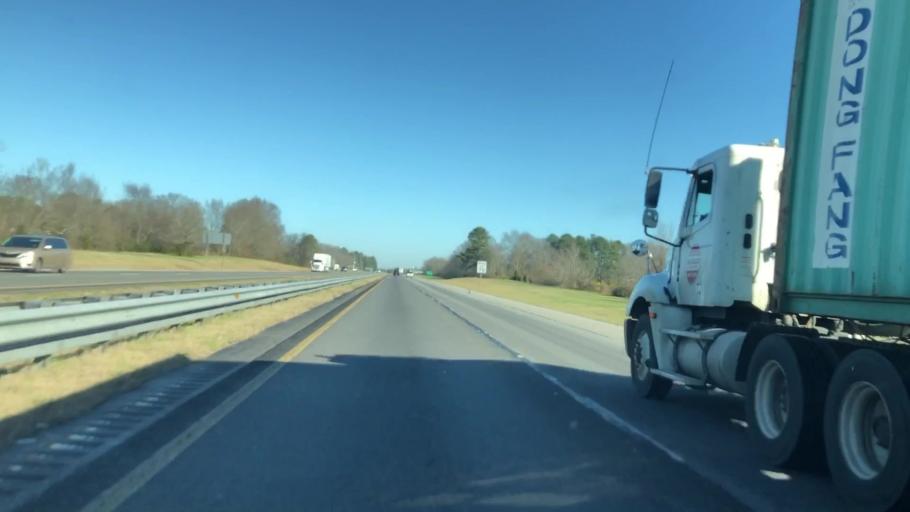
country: US
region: Alabama
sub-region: Limestone County
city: Athens
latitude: 34.8400
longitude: -86.9351
